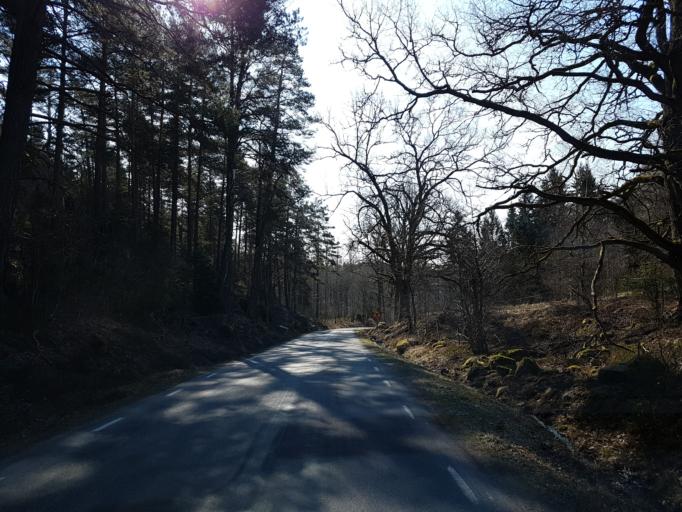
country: SE
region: Kalmar
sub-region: Vasterviks Kommun
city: Overum
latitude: 58.1525
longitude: 16.2289
